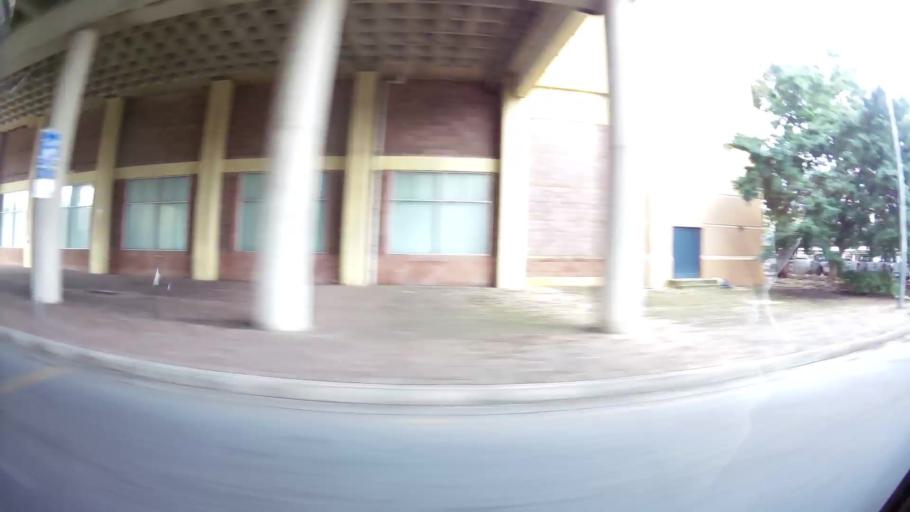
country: ZA
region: Eastern Cape
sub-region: Nelson Mandela Bay Metropolitan Municipality
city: Port Elizabeth
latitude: -33.9496
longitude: 25.5751
